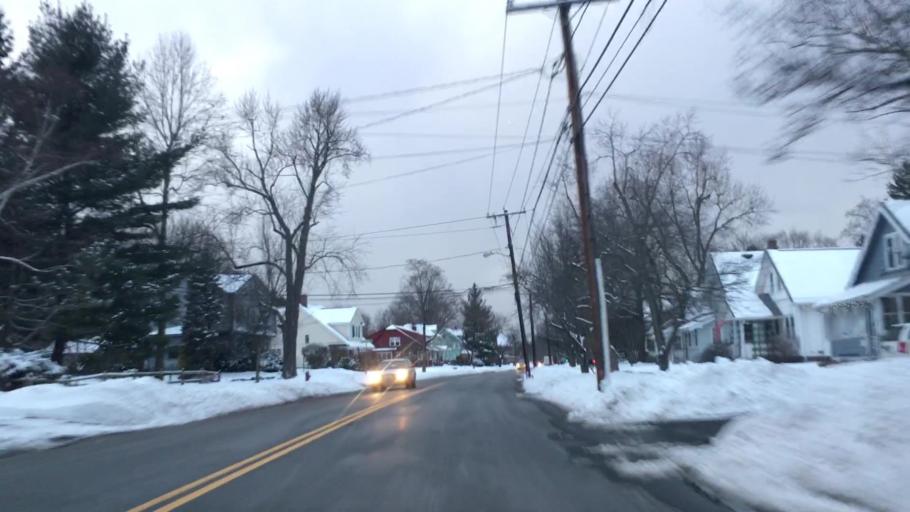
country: US
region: Massachusetts
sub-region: Hampden County
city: Longmeadow
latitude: 42.0573
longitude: -72.5745
